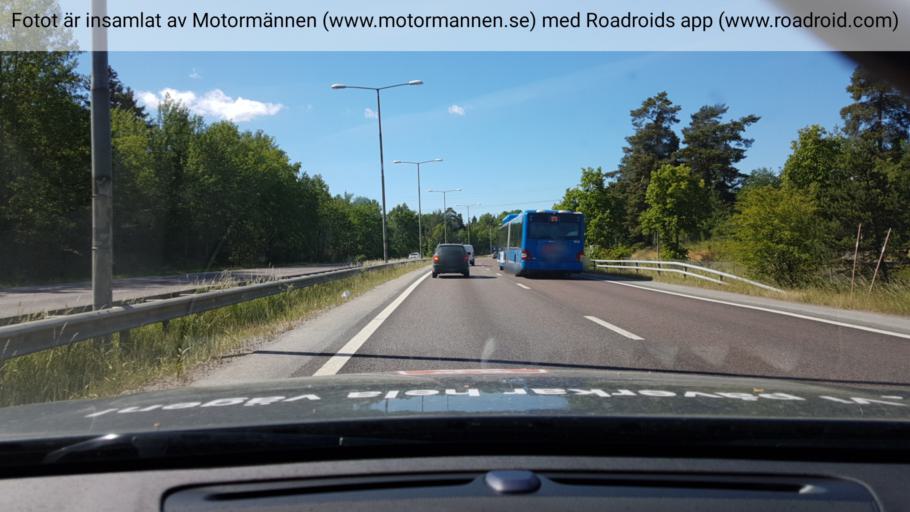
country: SE
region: Stockholm
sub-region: Stockholms Kommun
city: Arsta
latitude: 59.2606
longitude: 18.0689
